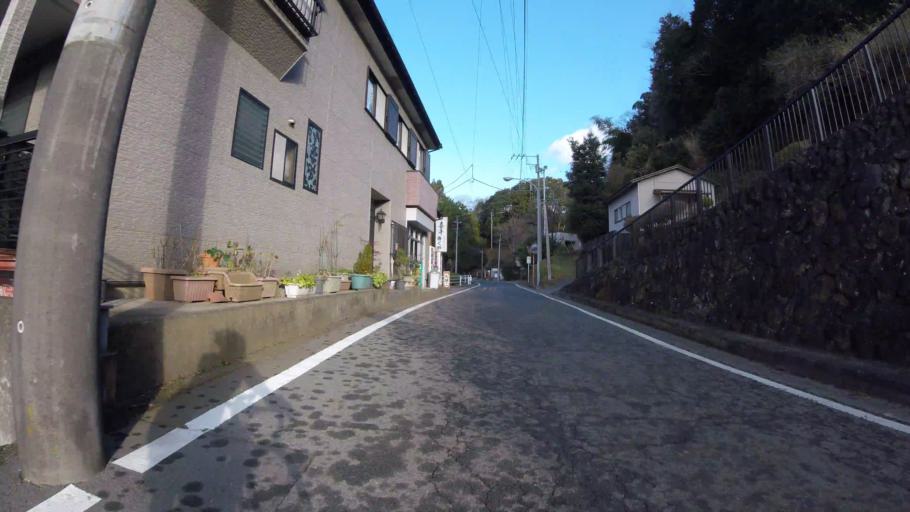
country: JP
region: Kanagawa
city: Yugawara
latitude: 35.1183
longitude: 139.0170
